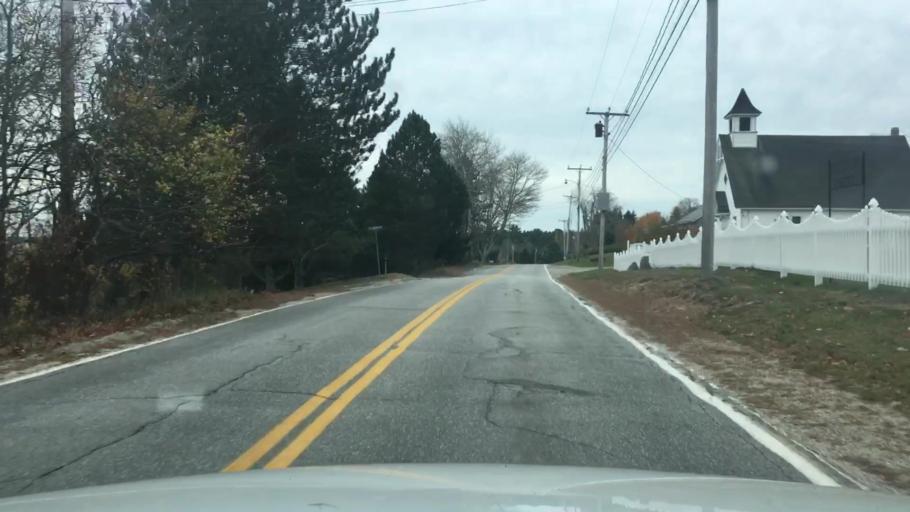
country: US
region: Maine
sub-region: Hancock County
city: Sedgwick
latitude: 44.3513
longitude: -68.5512
